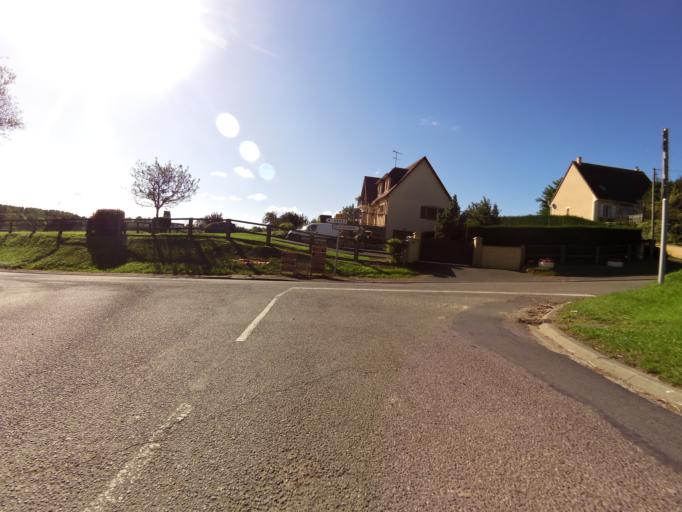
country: FR
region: Lower Normandy
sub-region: Departement du Calvados
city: Canon
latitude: 49.0467
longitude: -0.1269
